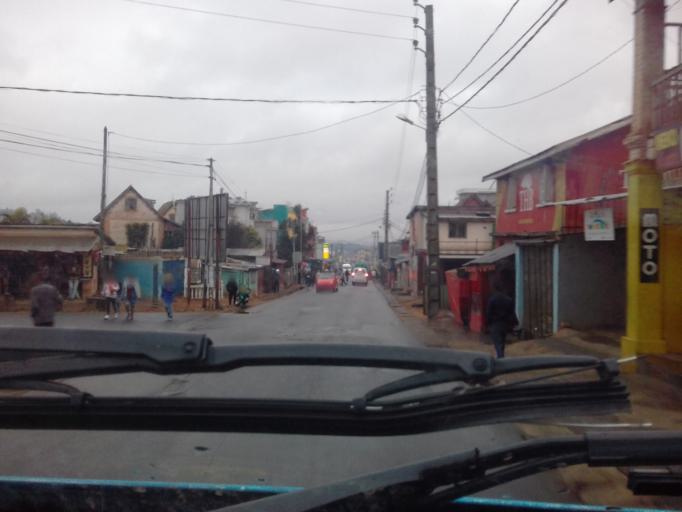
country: MG
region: Analamanga
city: Antananarivo
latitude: -18.8755
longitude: 47.5482
